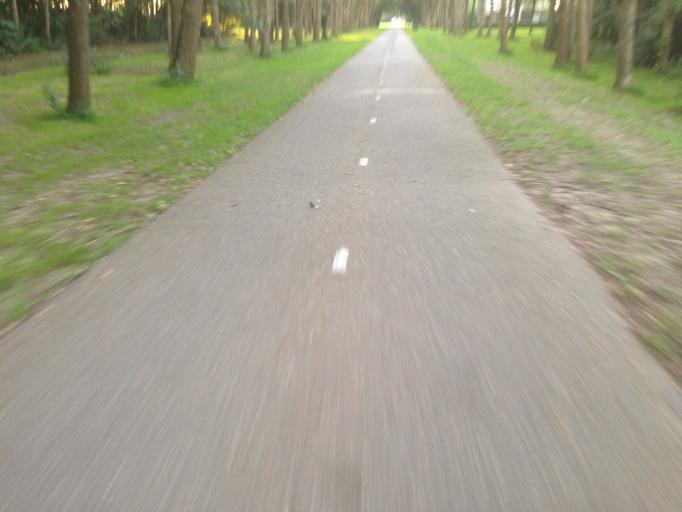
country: NL
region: Flevoland
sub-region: Gemeente Almere
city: Almere Stad
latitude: 52.3899
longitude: 5.2936
